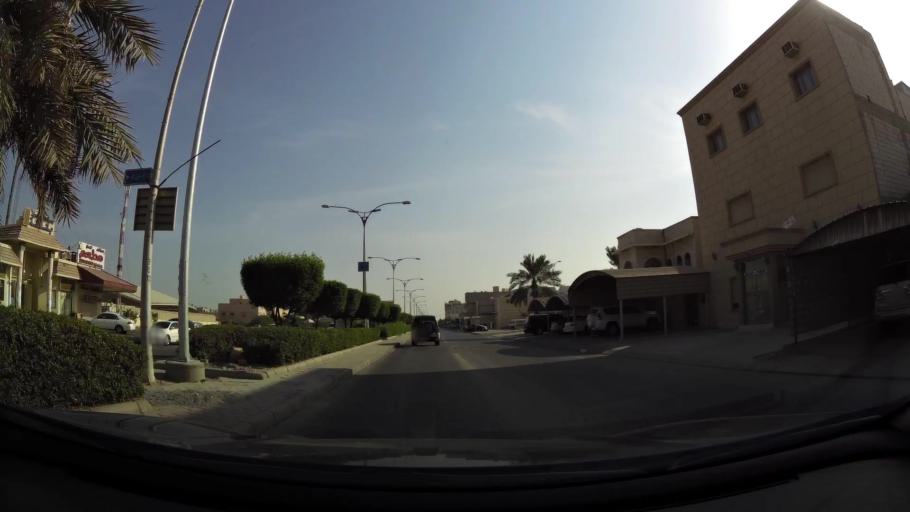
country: KW
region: Al Ahmadi
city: Ar Riqqah
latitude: 29.1405
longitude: 48.1079
